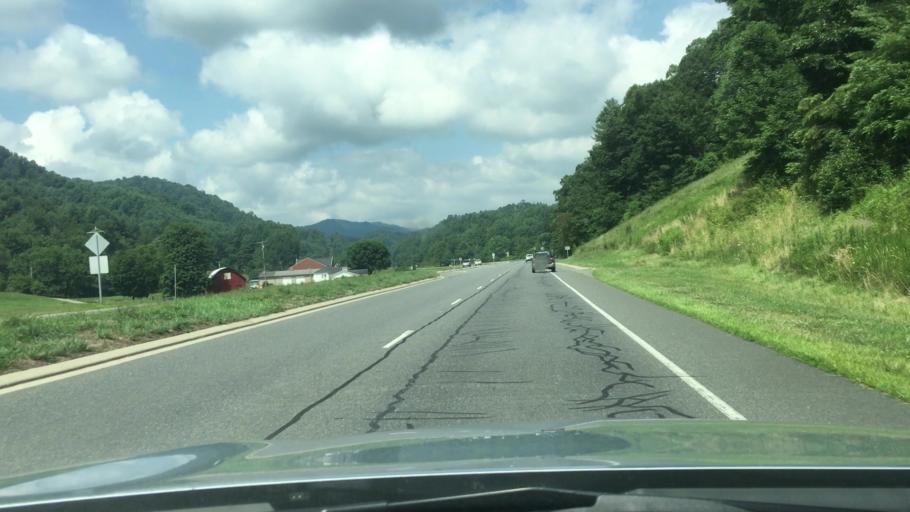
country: US
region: North Carolina
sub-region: Yancey County
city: Burnsville
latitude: 35.9137
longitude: -82.4258
